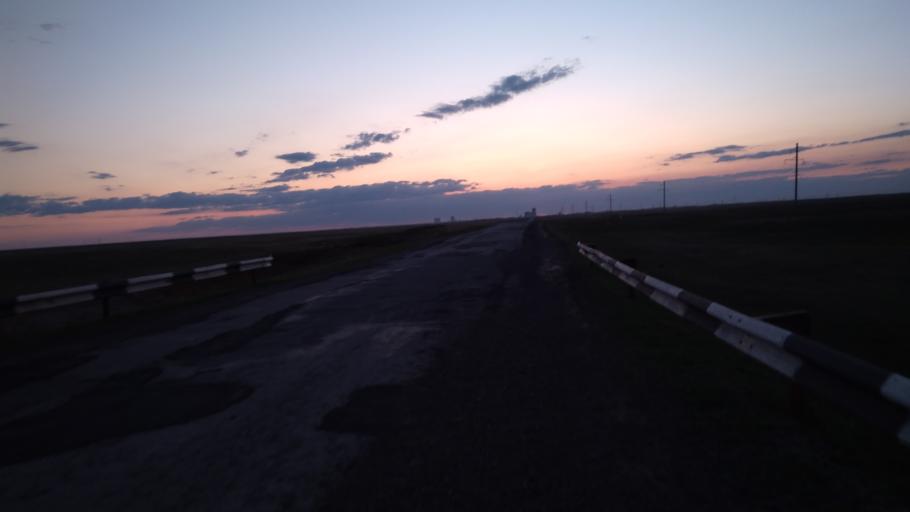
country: RU
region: Chelyabinsk
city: Troitsk
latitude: 54.0882
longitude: 61.6540
